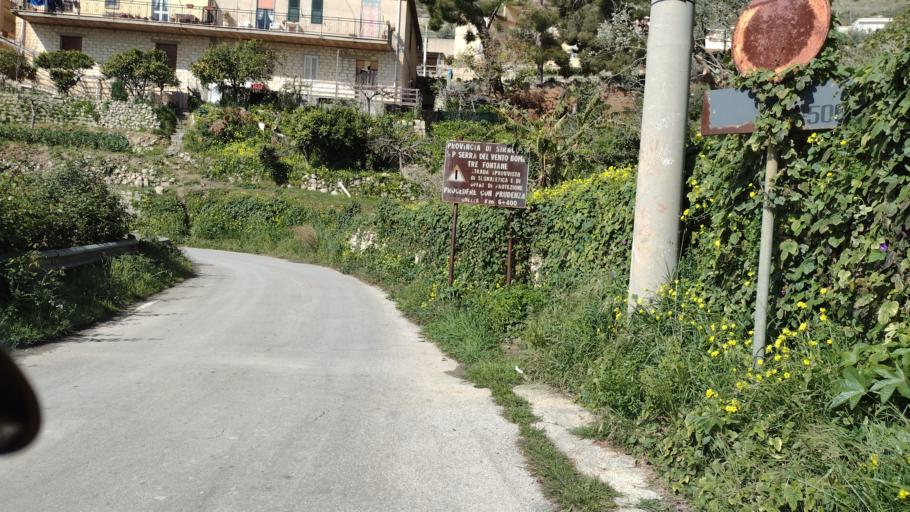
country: IT
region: Sicily
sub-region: Provincia di Siracusa
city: Noto
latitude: 36.9079
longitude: 15.0266
